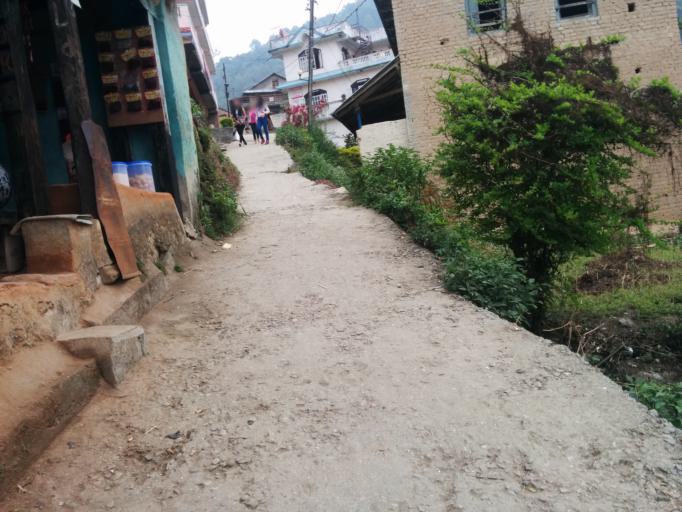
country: NP
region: Central Region
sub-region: Bagmati Zone
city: Bhaktapur
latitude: 27.7631
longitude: 85.4227
